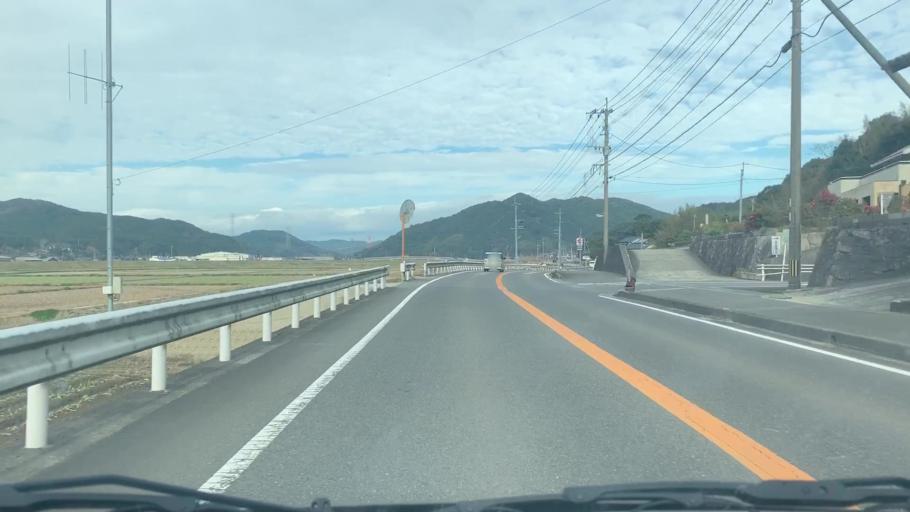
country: JP
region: Saga Prefecture
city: Karatsu
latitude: 33.3663
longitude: 130.0056
